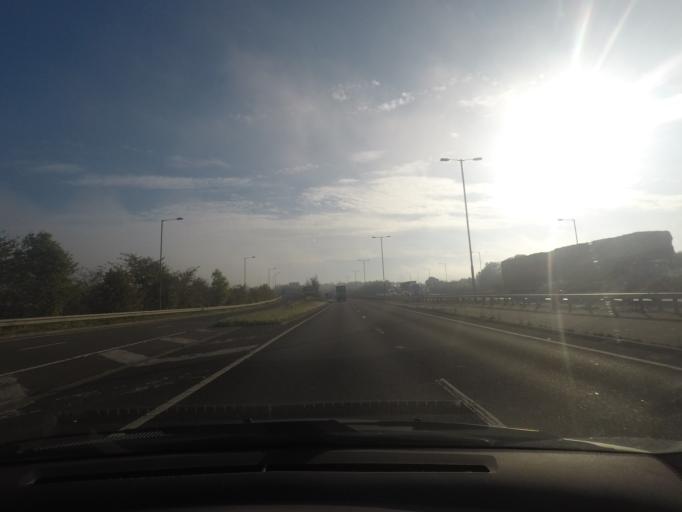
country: GB
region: England
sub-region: East Riding of Yorkshire
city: North Ferriby
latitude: 53.7249
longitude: -0.5253
